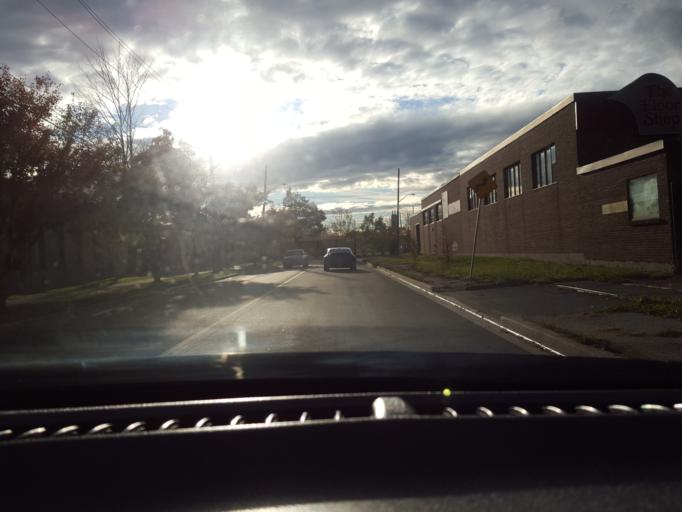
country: CA
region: Ontario
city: Toronto
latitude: 43.7119
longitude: -79.3551
